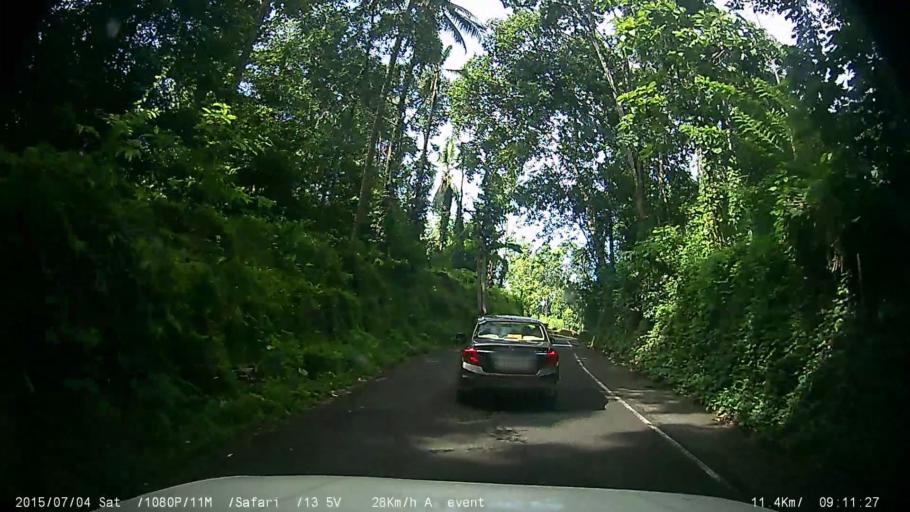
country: IN
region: Kerala
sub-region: Kottayam
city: Palackattumala
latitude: 9.7283
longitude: 76.6081
